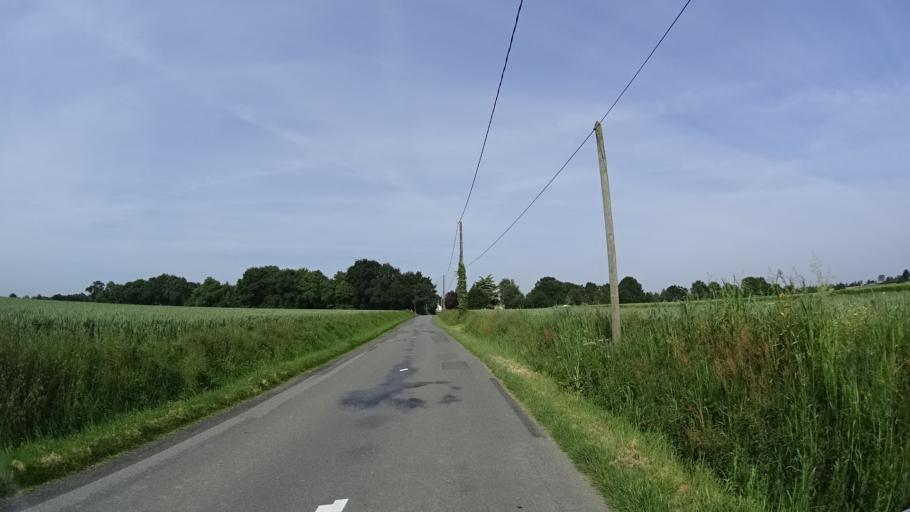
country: FR
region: Brittany
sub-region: Departement d'Ille-et-Vilaine
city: Chateaugiron
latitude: 48.0356
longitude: -1.5169
